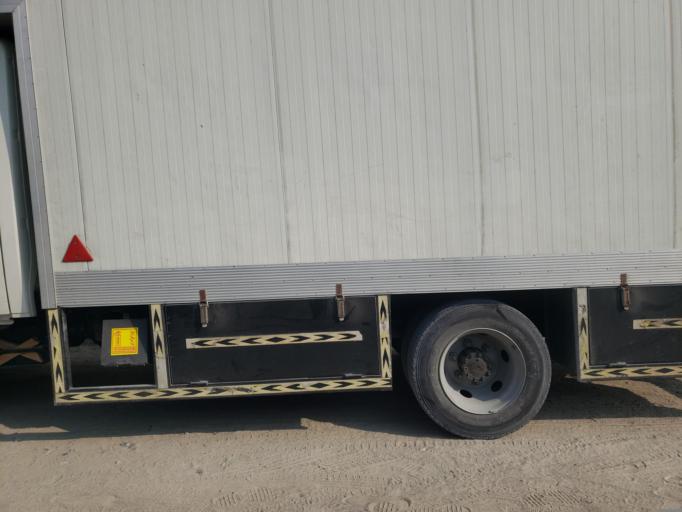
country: AE
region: Dubai
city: Dubai
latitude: 24.9856
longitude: 55.1097
